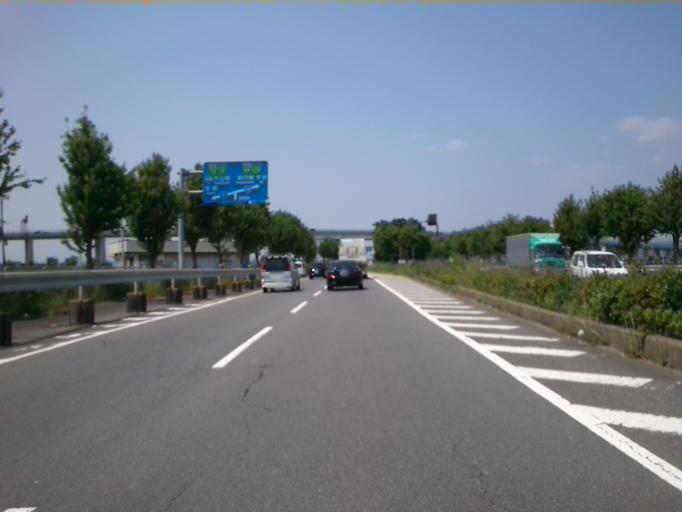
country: JP
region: Kyoto
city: Uji
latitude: 34.8996
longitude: 135.7637
